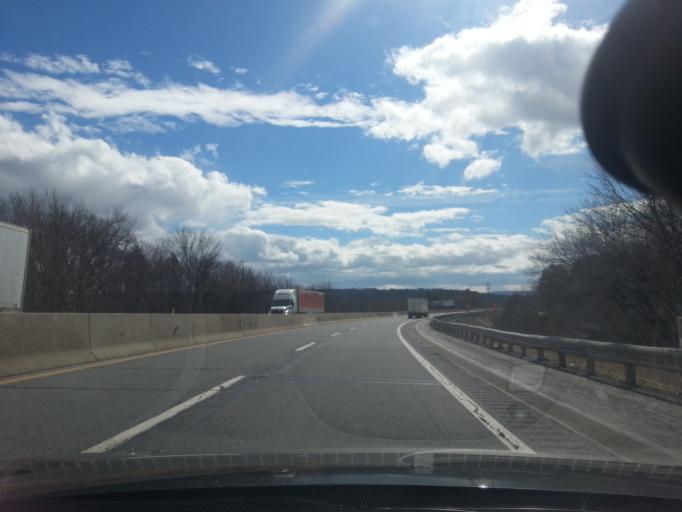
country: US
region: Pennsylvania
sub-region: Carbon County
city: Weissport East
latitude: 40.8592
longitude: -75.6499
